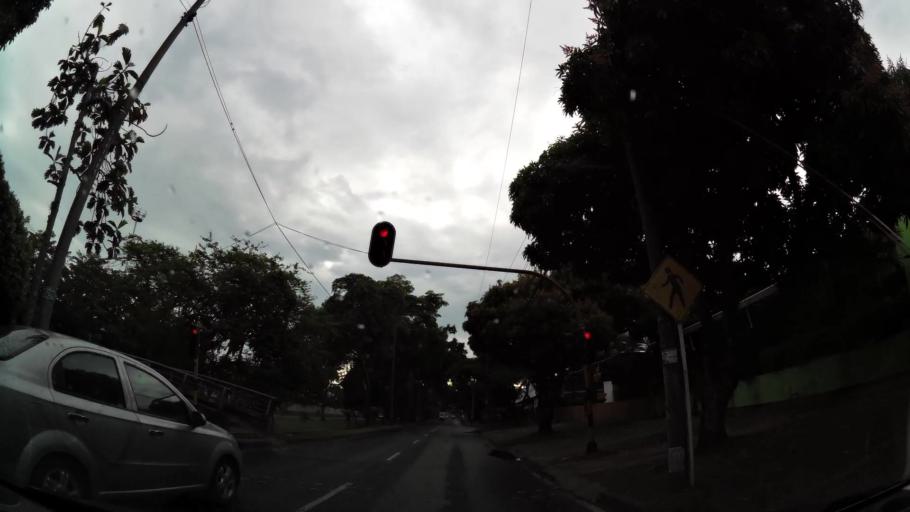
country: CO
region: Valle del Cauca
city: Cali
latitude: 3.4868
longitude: -76.5186
